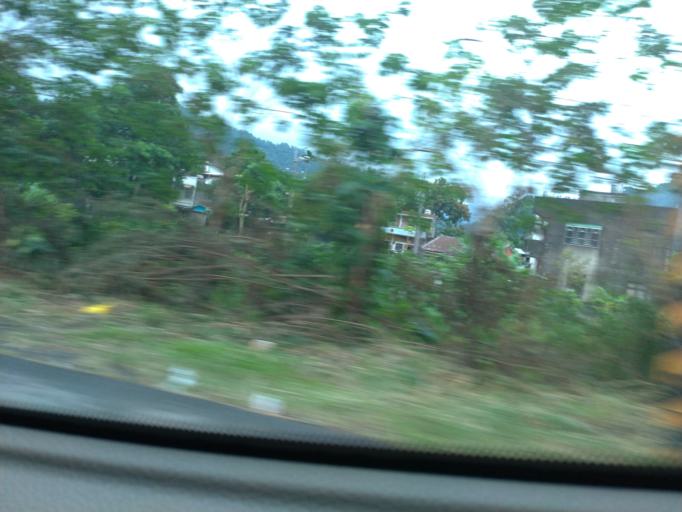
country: TW
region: Taipei
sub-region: Taipei
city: Banqiao
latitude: 24.9328
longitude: 121.4060
